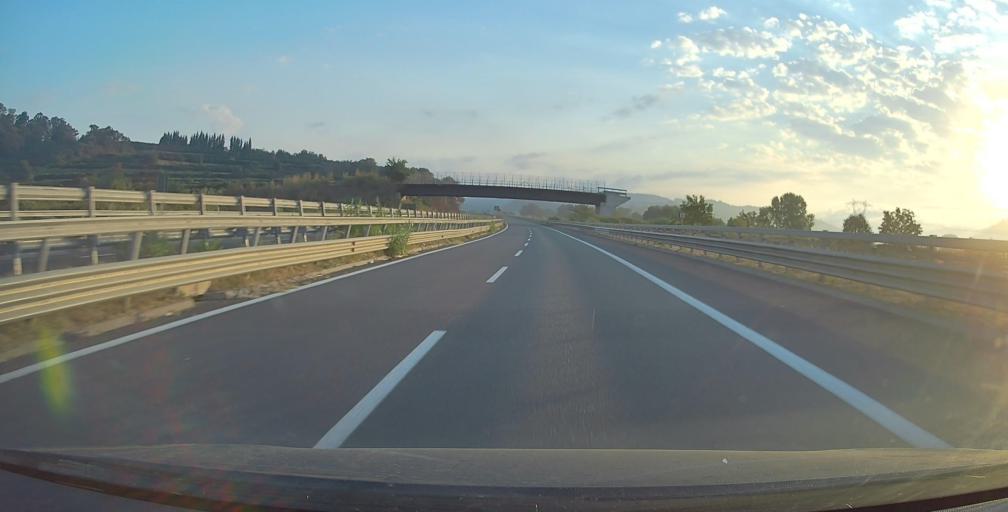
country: IT
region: Calabria
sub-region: Provincia di Reggio Calabria
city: Candidoni
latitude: 38.5138
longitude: 16.0491
